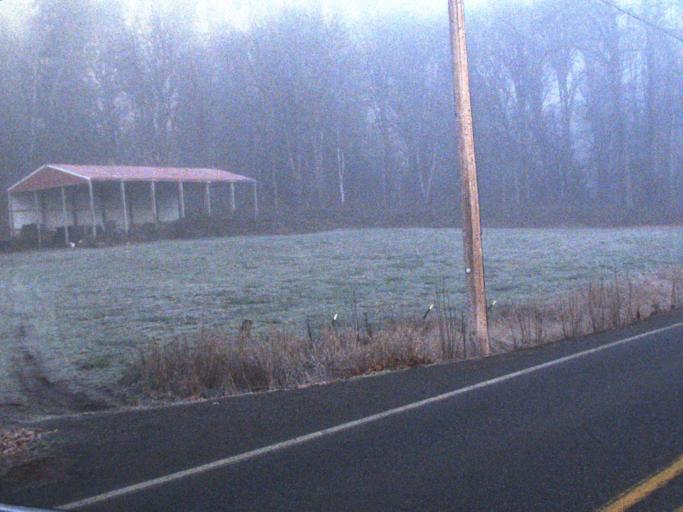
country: US
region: Washington
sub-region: Snohomish County
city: Darrington
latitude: 48.4900
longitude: -121.5767
